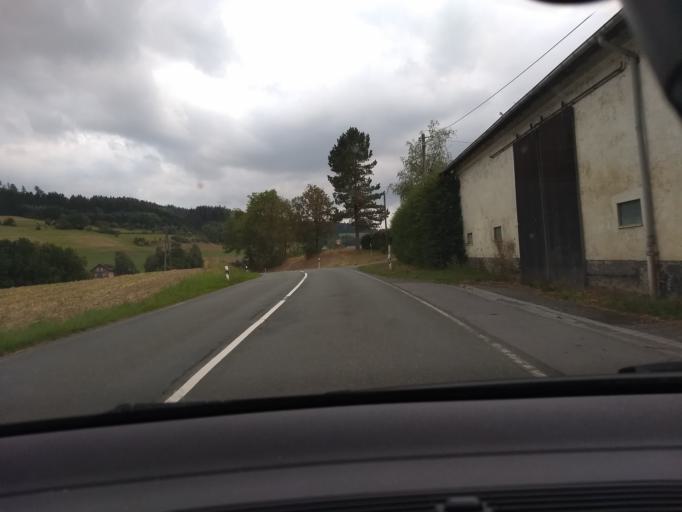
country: DE
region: North Rhine-Westphalia
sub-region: Regierungsbezirk Arnsberg
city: Arnsberg
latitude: 51.3496
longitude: 8.1317
